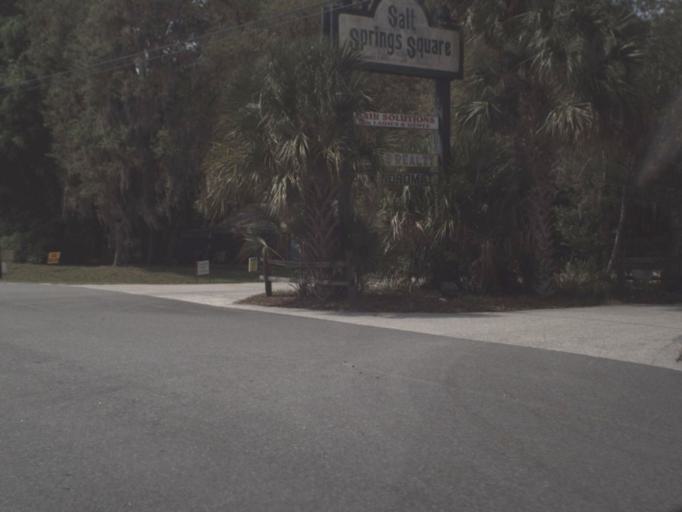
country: US
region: Florida
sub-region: Putnam County
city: Crescent City
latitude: 29.3585
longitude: -81.7353
